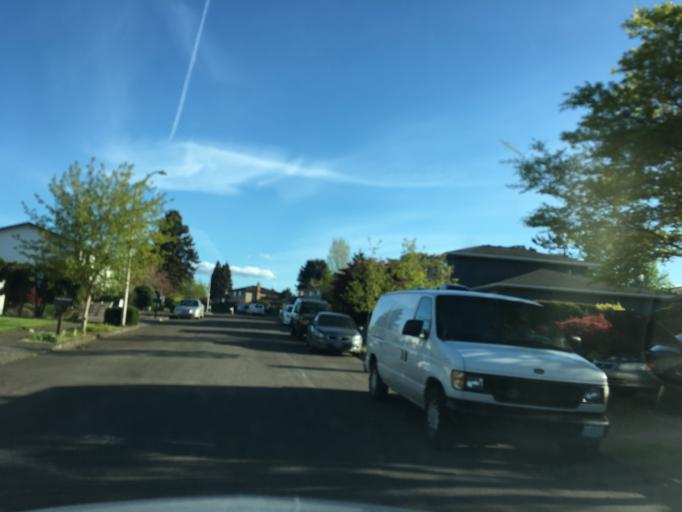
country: US
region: Oregon
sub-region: Multnomah County
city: Lents
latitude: 45.5534
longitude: -122.5300
